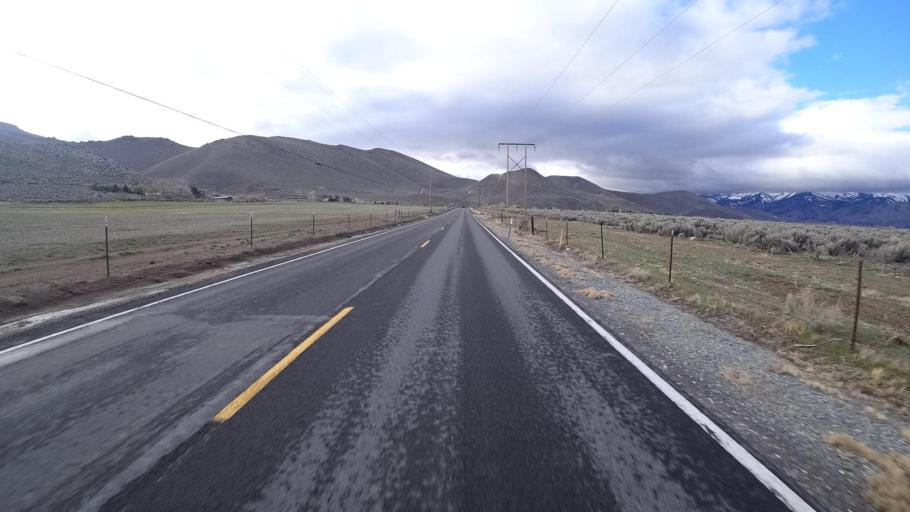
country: US
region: Nevada
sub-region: Carson City
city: Carson City
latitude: 39.2517
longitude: -119.7567
